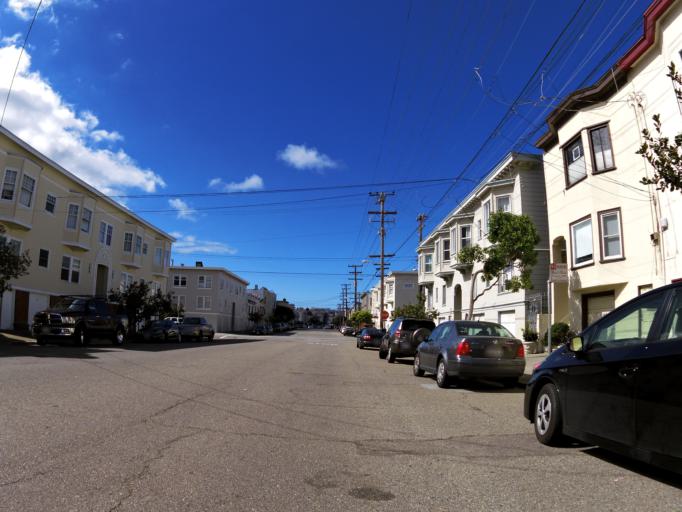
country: US
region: California
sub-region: San Francisco County
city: San Francisco
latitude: 37.7786
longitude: -122.4765
